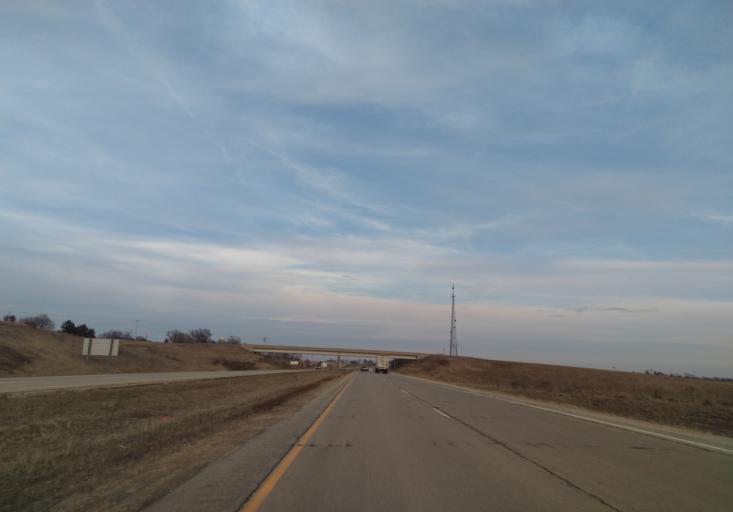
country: US
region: Wisconsin
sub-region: Dane County
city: Mount Horeb
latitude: 43.0046
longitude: -89.6943
